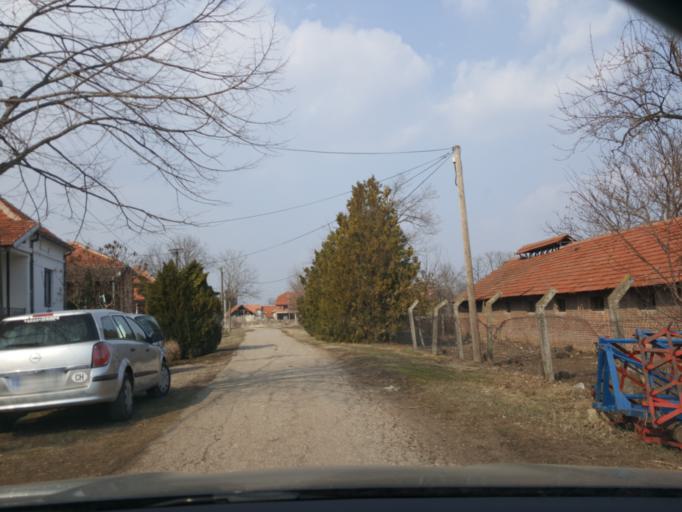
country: RS
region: Central Serbia
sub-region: Nisavski Okrug
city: Aleksinac
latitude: 43.4229
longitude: 21.7860
